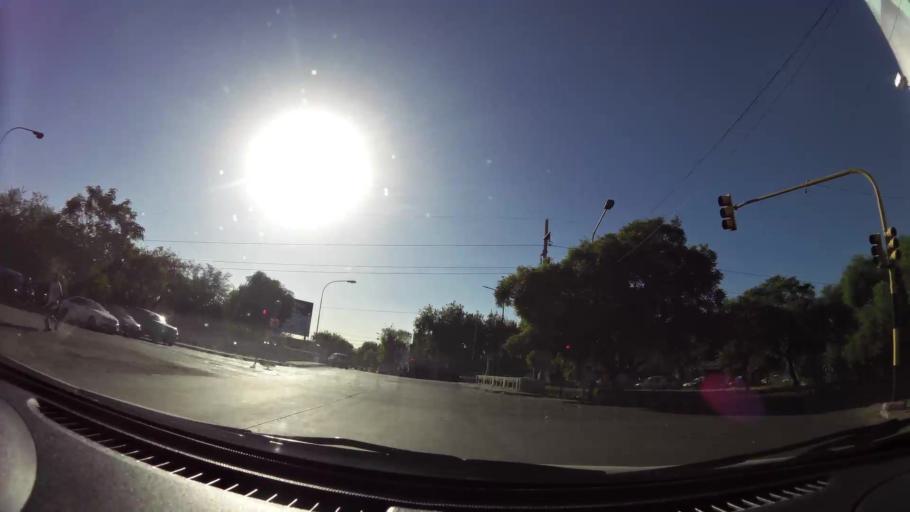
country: AR
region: Mendoza
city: Mendoza
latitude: -32.9045
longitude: -68.8380
